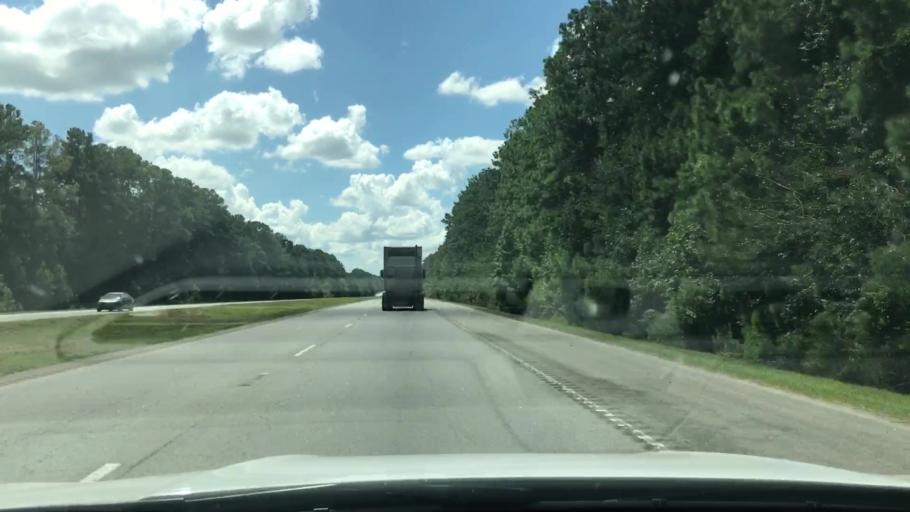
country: US
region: South Carolina
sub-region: Berkeley County
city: Hanahan
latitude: 32.9446
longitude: -79.9990
